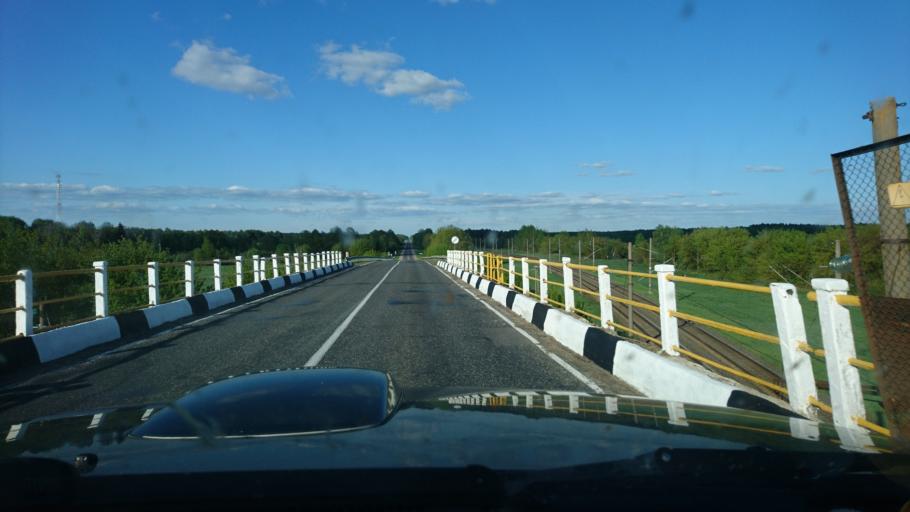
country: BY
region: Brest
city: Nyakhachava
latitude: 52.6392
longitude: 25.1958
